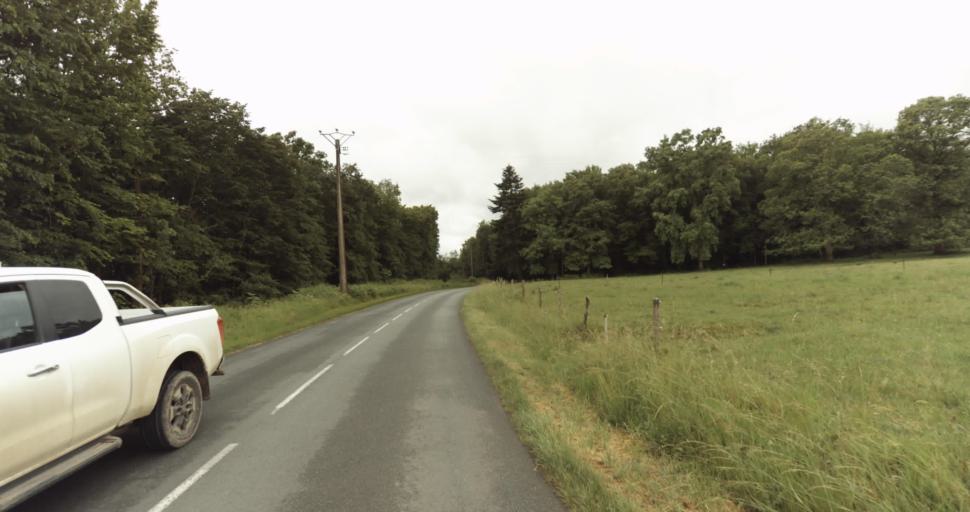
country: FR
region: Aquitaine
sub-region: Departement de la Dordogne
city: Belves
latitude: 44.6931
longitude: 0.9112
